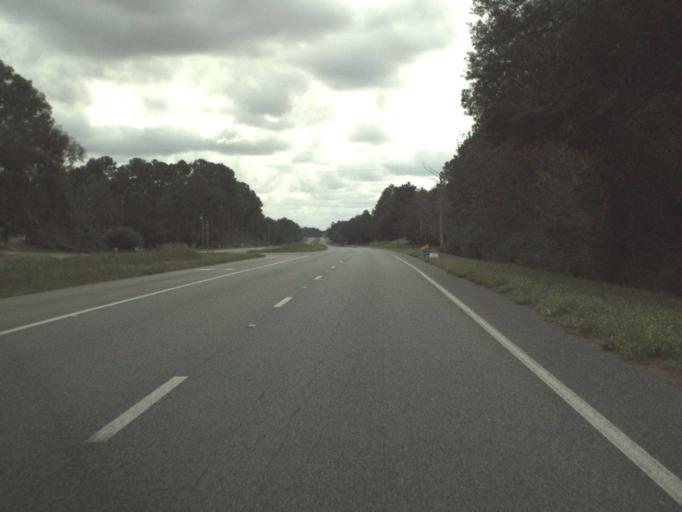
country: US
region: Florida
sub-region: Jefferson County
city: Monticello
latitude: 30.6080
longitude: -83.8723
